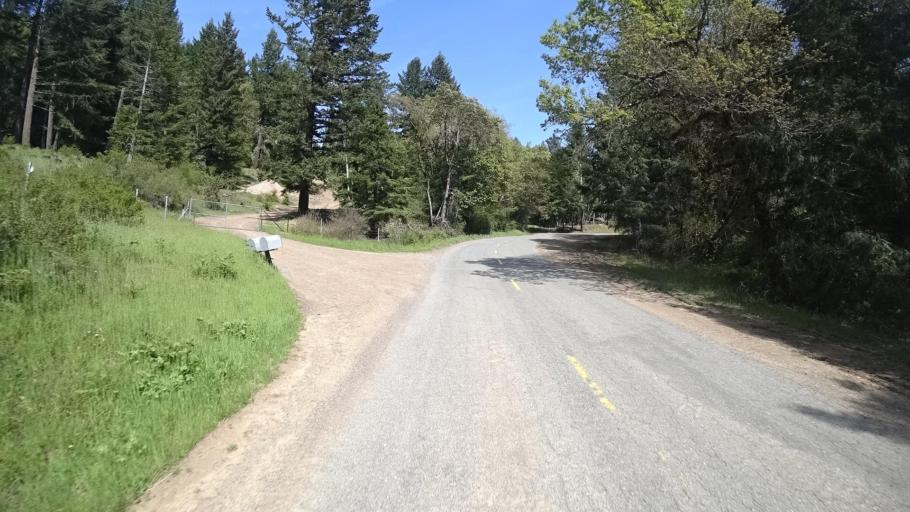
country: US
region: California
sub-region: Humboldt County
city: Redway
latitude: 40.3506
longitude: -123.7156
